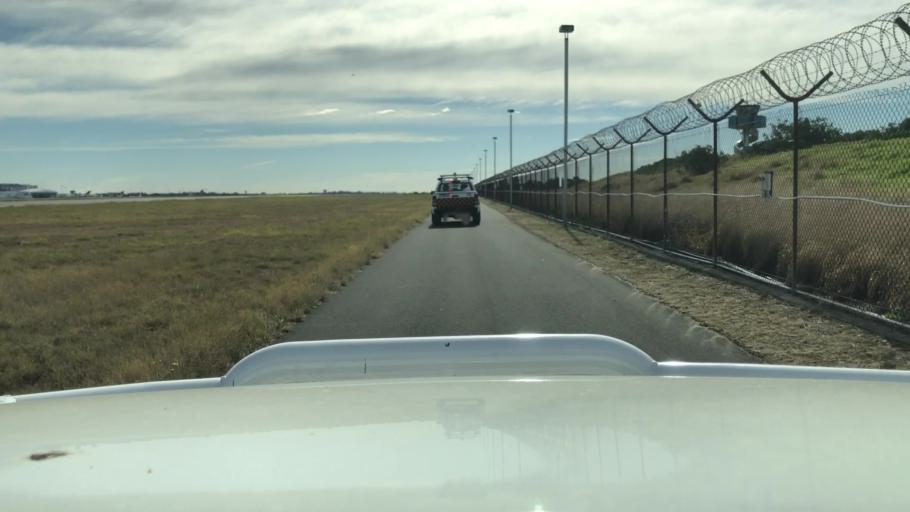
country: AU
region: New South Wales
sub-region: Botany Bay
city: Botany
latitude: -33.9493
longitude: 151.1804
